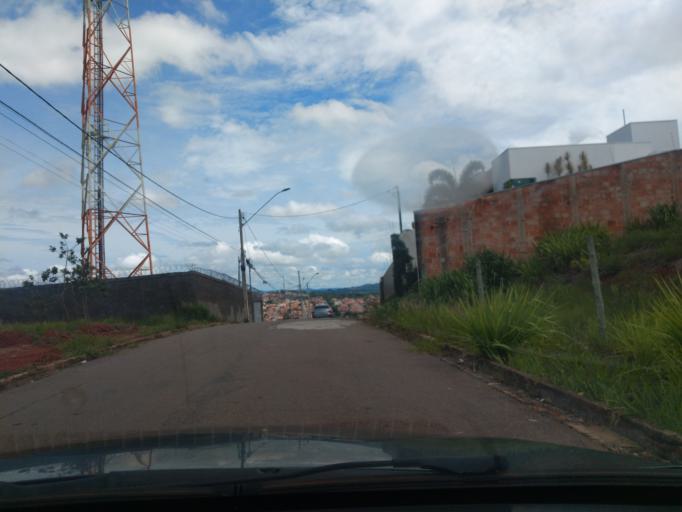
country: BR
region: Minas Gerais
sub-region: Tres Coracoes
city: Tres Coracoes
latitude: -21.6705
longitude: -45.2770
